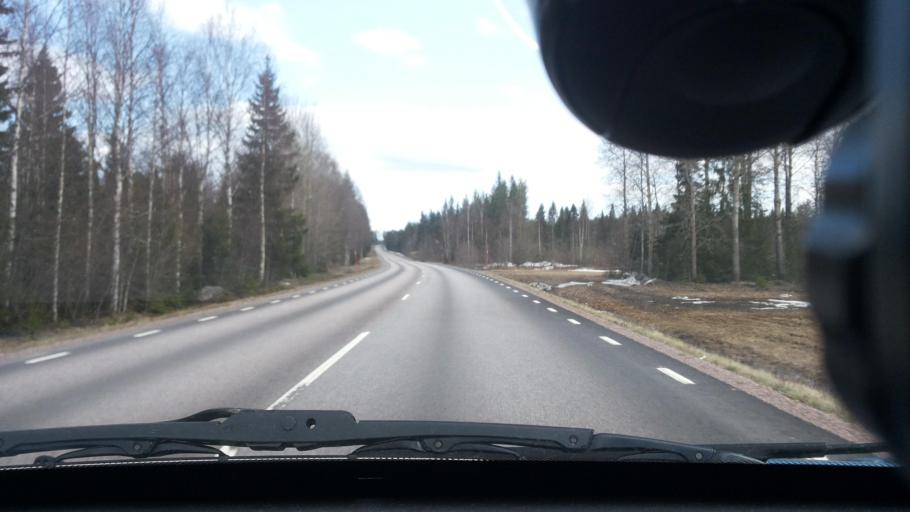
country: SE
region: Norrbotten
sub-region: Lulea Kommun
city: Gammelstad
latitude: 65.6059
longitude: 21.9656
